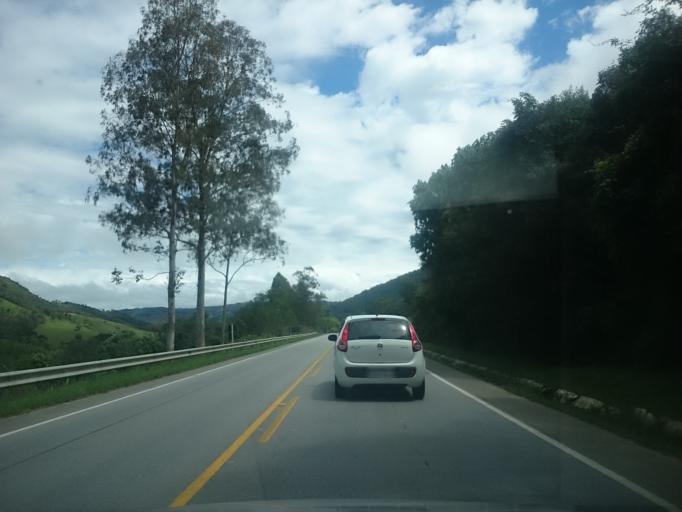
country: BR
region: Santa Catarina
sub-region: Anitapolis
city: Anitapolis
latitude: -27.6898
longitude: -49.2285
